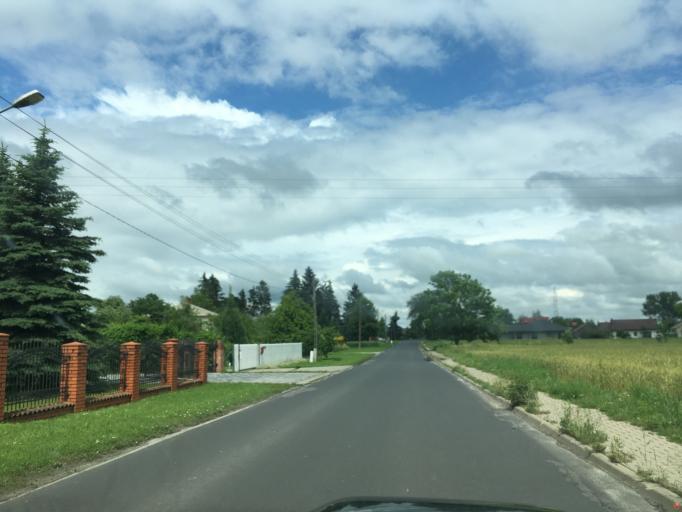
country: PL
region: Lublin Voivodeship
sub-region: Powiat swidnicki
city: Swidnik
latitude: 51.2030
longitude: 22.7335
